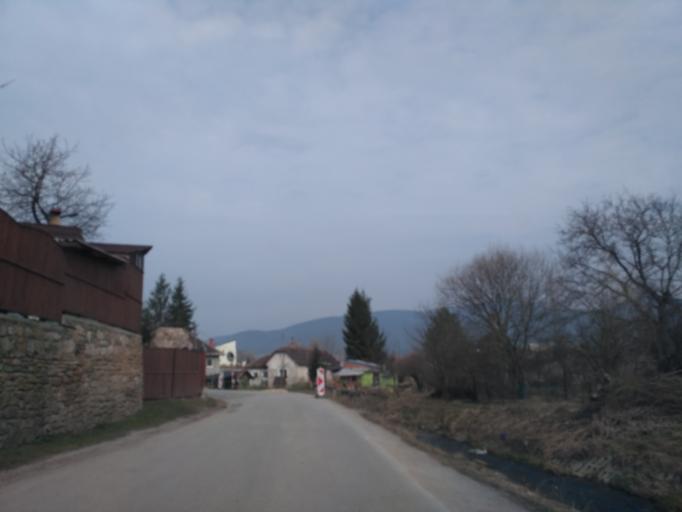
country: SK
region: Kosicky
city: Roznava
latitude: 48.6331
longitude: 20.4981
